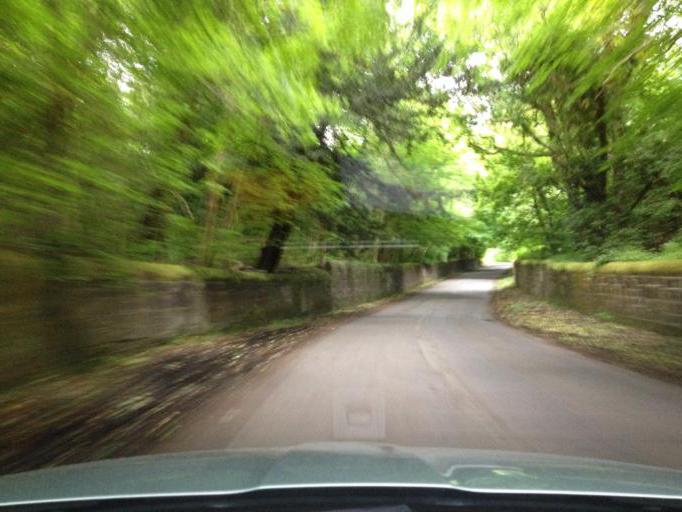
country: GB
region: Scotland
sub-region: West Dunbartonshire
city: Old Kilpatrick
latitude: 55.9158
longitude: -4.4624
